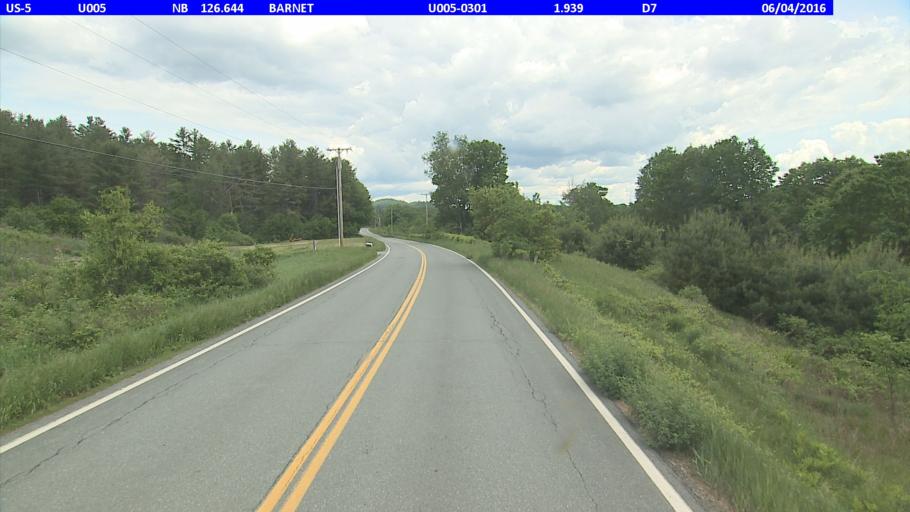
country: US
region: New Hampshire
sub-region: Grafton County
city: Woodsville
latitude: 44.2818
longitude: -72.0636
